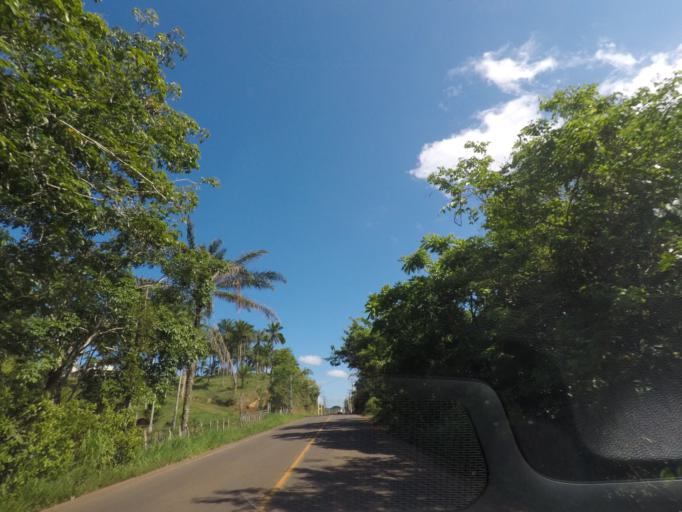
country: BR
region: Bahia
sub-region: Camamu
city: Camamu
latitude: -13.9307
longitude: -39.1131
